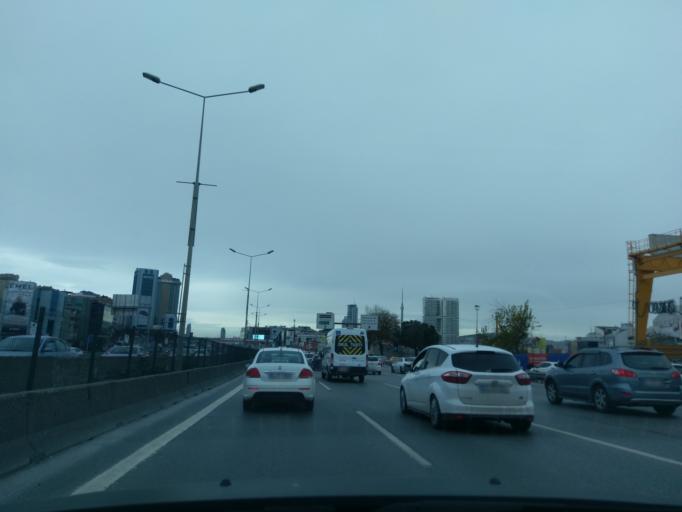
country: TR
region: Istanbul
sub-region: Atasehir
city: Atasehir
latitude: 40.9841
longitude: 29.0921
